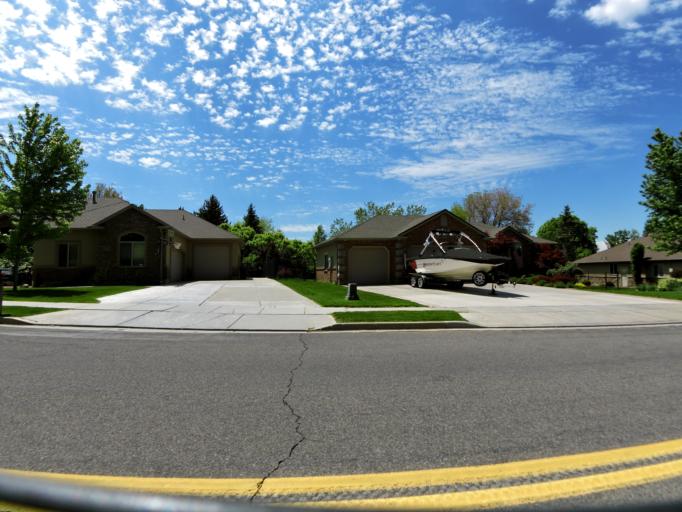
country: US
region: Utah
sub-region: Weber County
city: Uintah
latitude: 41.1779
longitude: -111.9306
